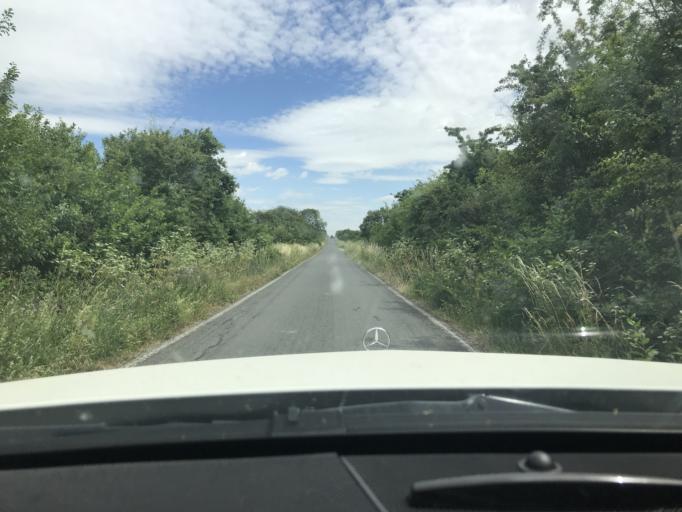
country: DE
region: Thuringia
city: Urbach
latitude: 51.2947
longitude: 10.6258
